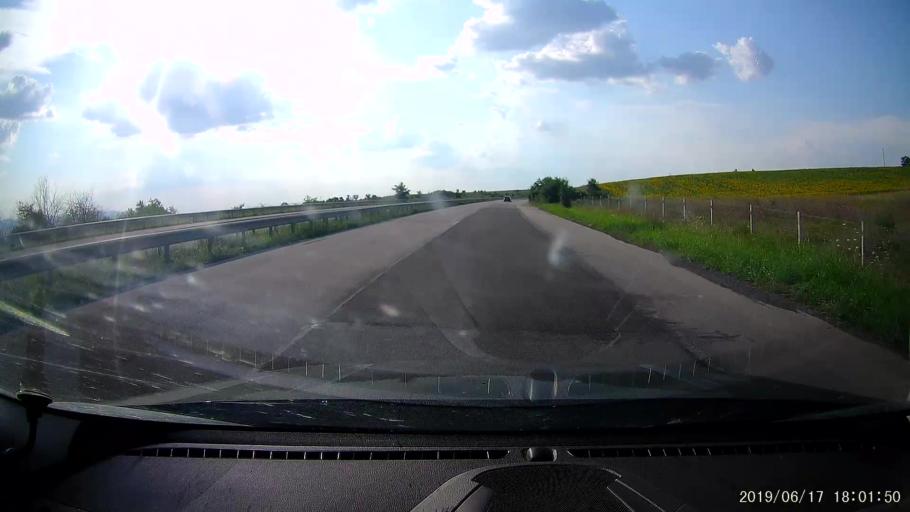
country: BG
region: Khaskovo
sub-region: Obshtina Svilengrad
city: Svilengrad
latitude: 41.7491
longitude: 26.2431
